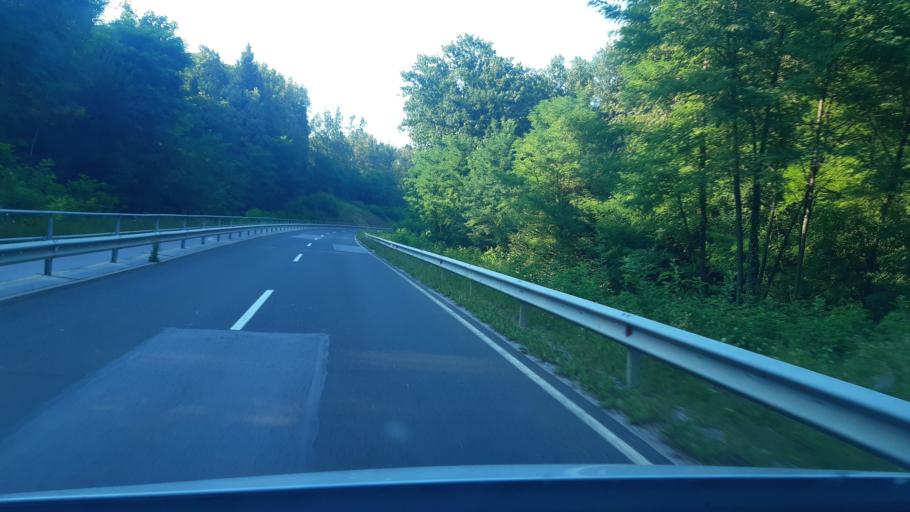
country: SI
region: Crnomelj
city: Crnomelj
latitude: 45.5796
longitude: 15.1815
